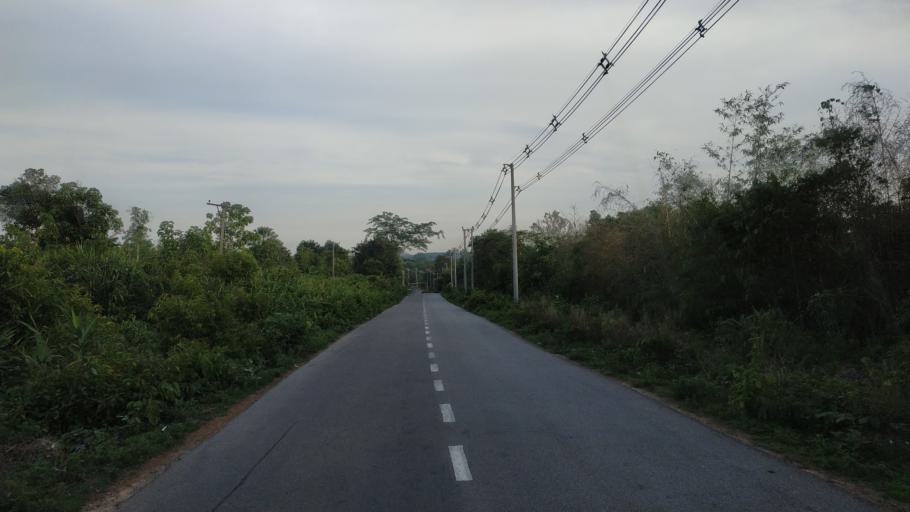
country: MM
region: Mon
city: Kyaikto
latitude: 17.4105
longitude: 97.0729
